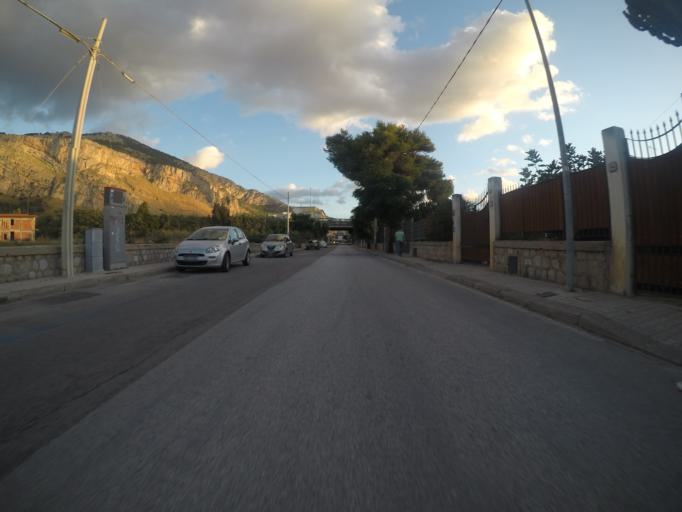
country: IT
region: Sicily
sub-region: Palermo
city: Capaci
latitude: 38.1826
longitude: 13.2380
